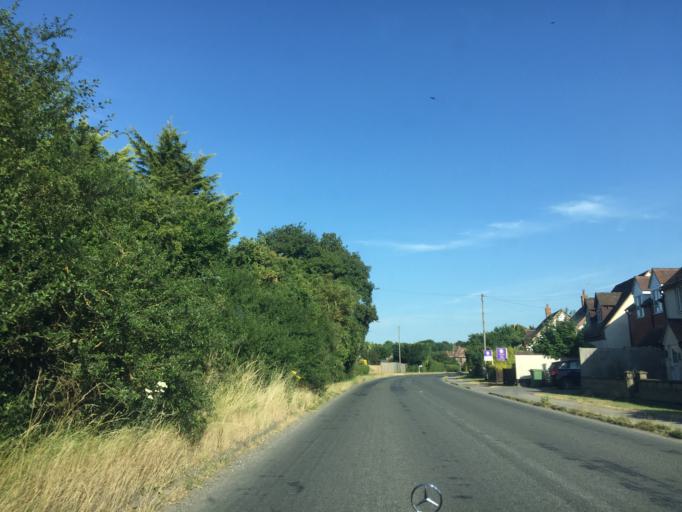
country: GB
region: England
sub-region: Oxfordshire
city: Thame
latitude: 51.7135
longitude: -1.0114
